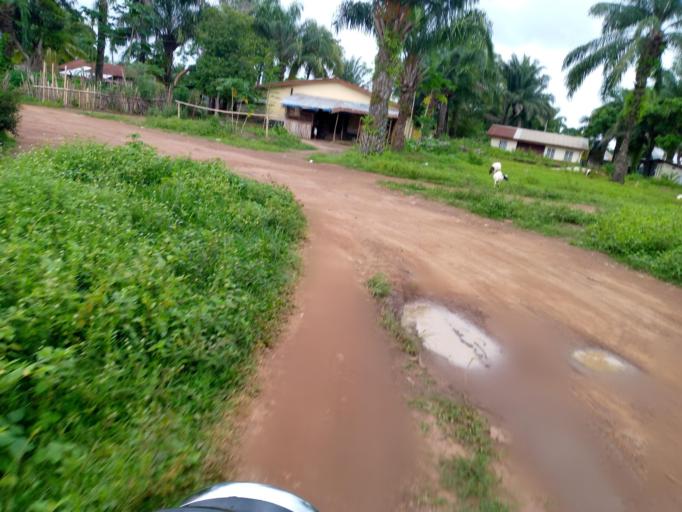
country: SL
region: Southern Province
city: Moyamba
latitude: 8.1529
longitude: -12.4363
